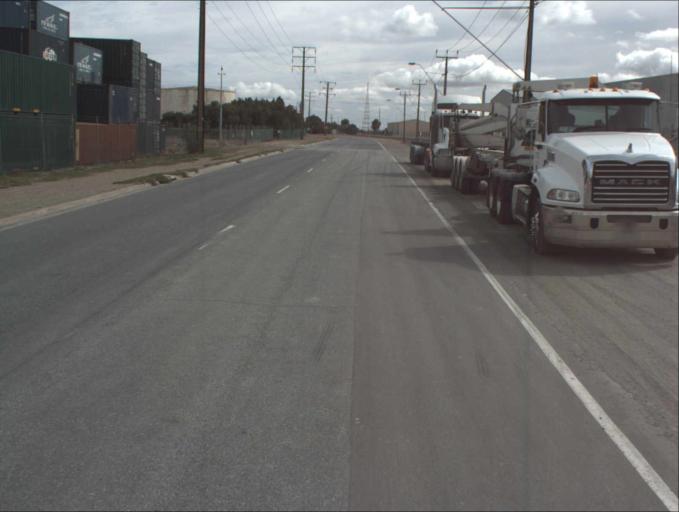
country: AU
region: South Australia
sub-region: Port Adelaide Enfield
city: Birkenhead
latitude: -34.8209
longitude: 138.5069
